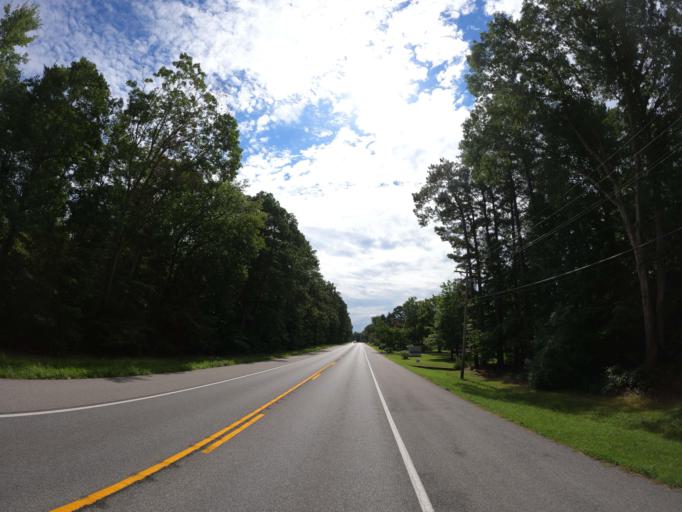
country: US
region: Maryland
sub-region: Saint Mary's County
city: Leonardtown
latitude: 38.2447
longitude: -76.5815
